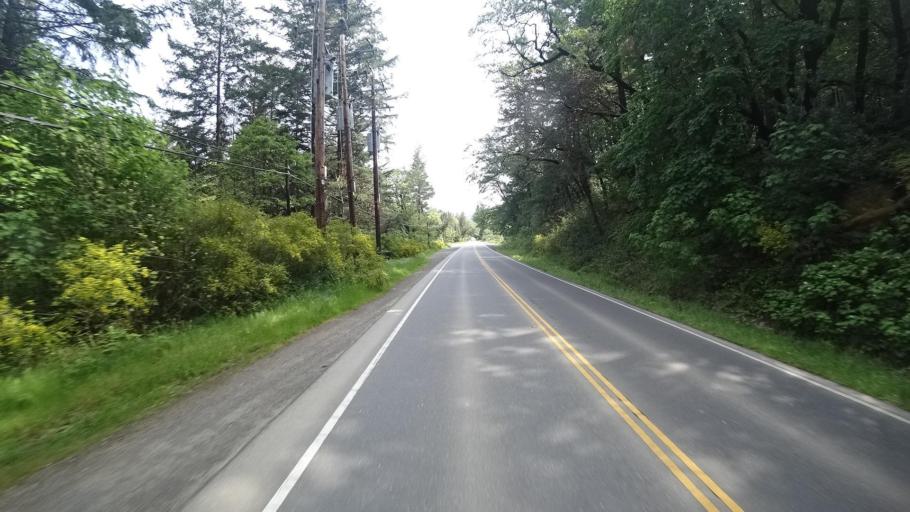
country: US
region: California
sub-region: Humboldt County
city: Redway
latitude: 40.1378
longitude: -123.8143
